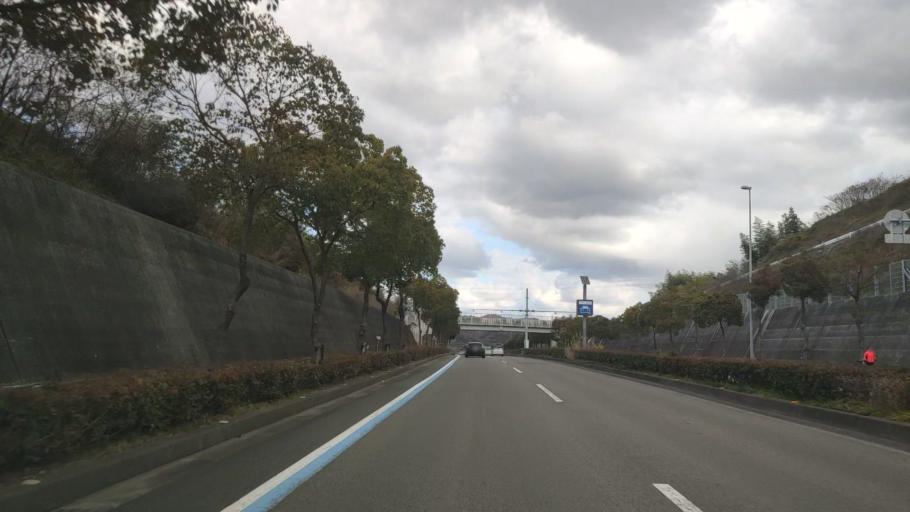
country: JP
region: Ehime
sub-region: Shikoku-chuo Shi
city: Matsuyama
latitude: 33.8900
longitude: 132.7568
